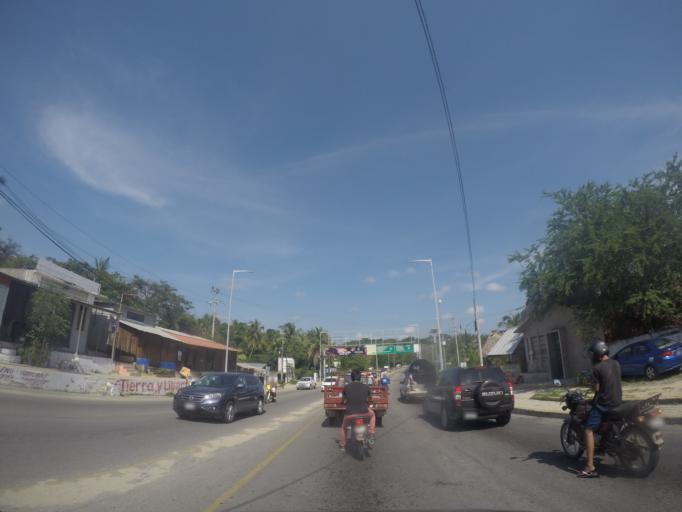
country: MX
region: Oaxaca
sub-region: San Pedro Mixtepec -Dto. 22 -
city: Puerto Escondido
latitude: 15.8624
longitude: -97.0610
